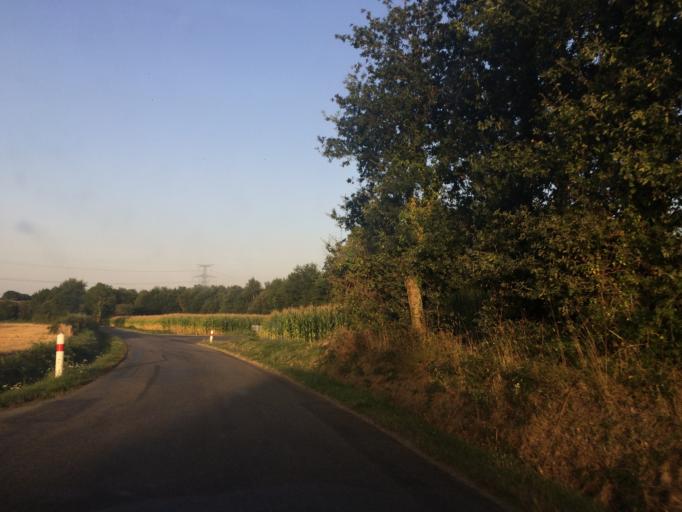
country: FR
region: Brittany
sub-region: Departement du Morbihan
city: Allaire
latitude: 47.6342
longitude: -2.1998
